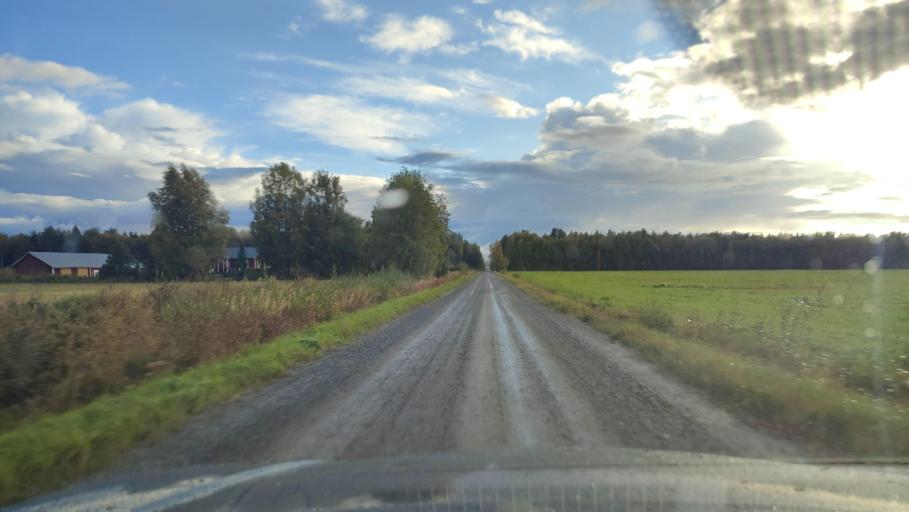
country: FI
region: Southern Ostrobothnia
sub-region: Suupohja
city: Karijoki
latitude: 62.3229
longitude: 21.5697
